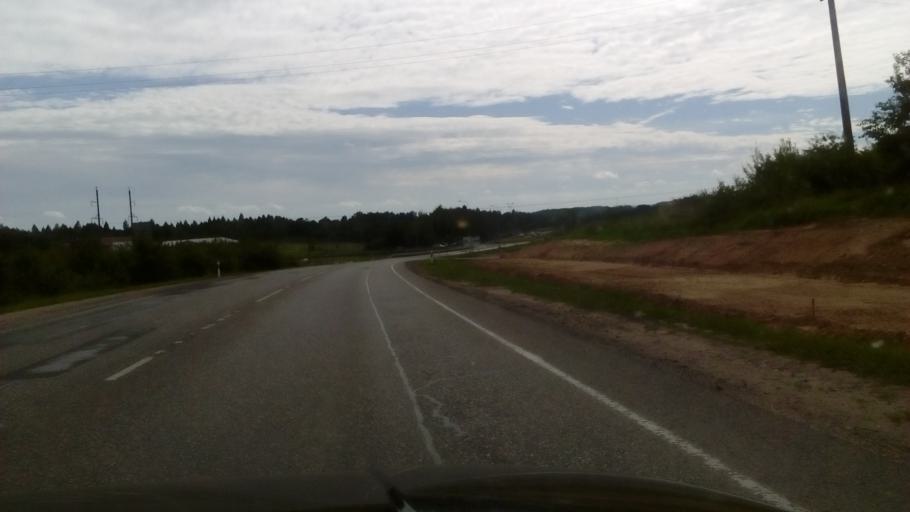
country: LT
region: Alytaus apskritis
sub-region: Alytus
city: Alytus
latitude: 54.3908
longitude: 23.9983
